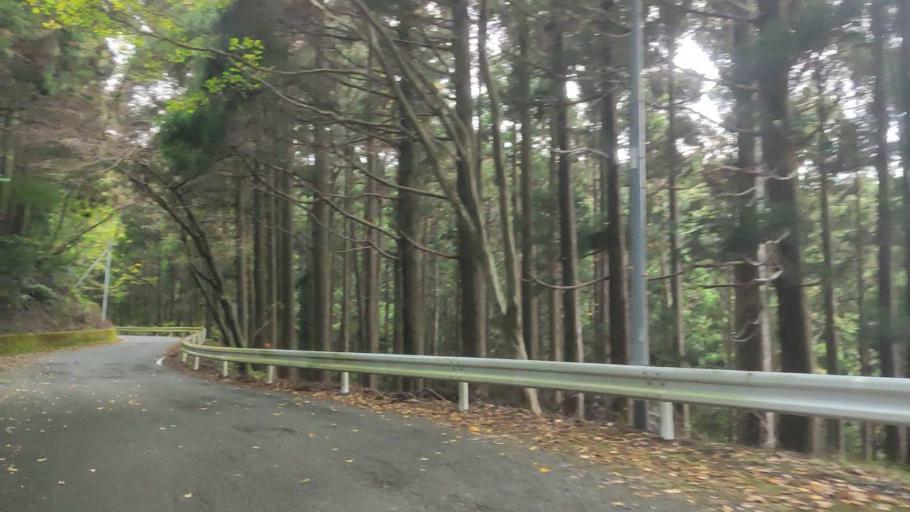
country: JP
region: Shizuoka
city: Ito
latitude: 34.9012
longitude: 138.9575
